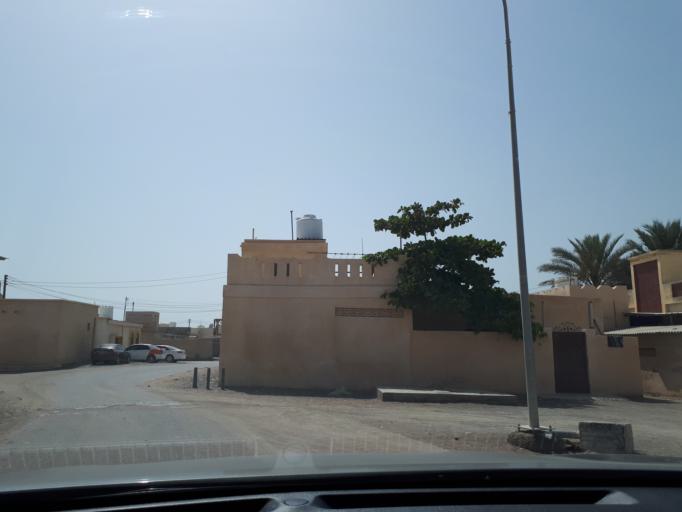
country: OM
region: Al Batinah
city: Barka'
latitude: 23.7063
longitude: 57.9275
